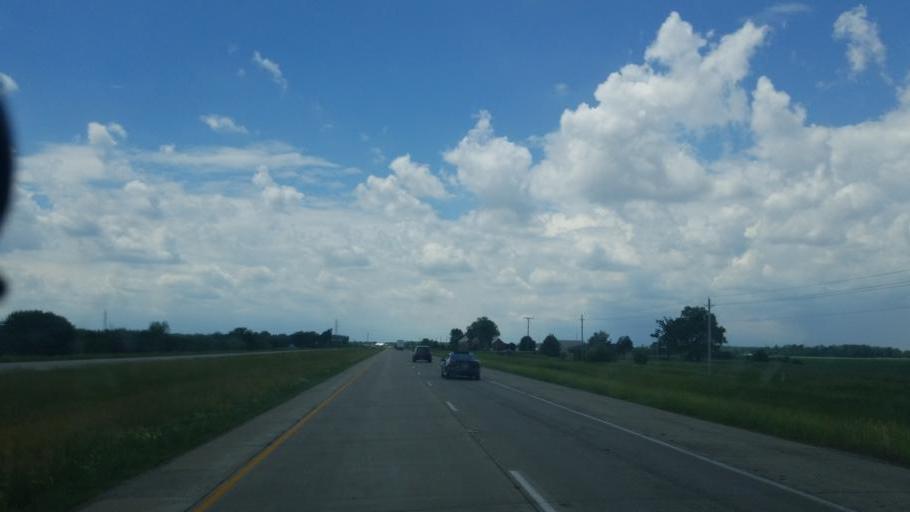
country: US
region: Indiana
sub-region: Allen County
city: New Haven
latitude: 41.0527
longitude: -84.9641
